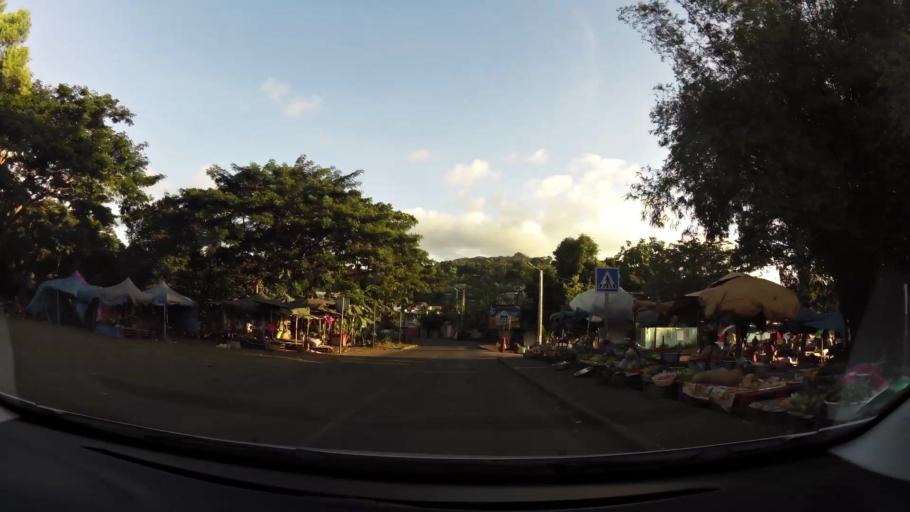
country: YT
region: Dembeni
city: Dembeni
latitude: -12.8421
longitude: 45.1840
